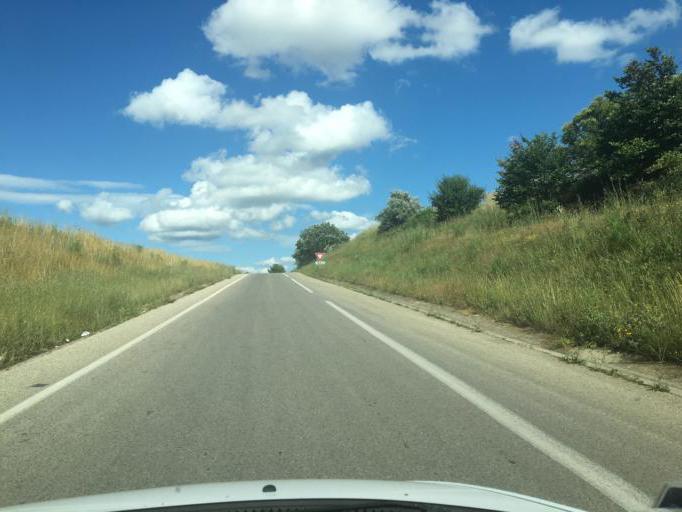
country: FR
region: Provence-Alpes-Cote d'Azur
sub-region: Departement des Bouches-du-Rhone
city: Eguilles
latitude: 43.5441
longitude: 5.3486
